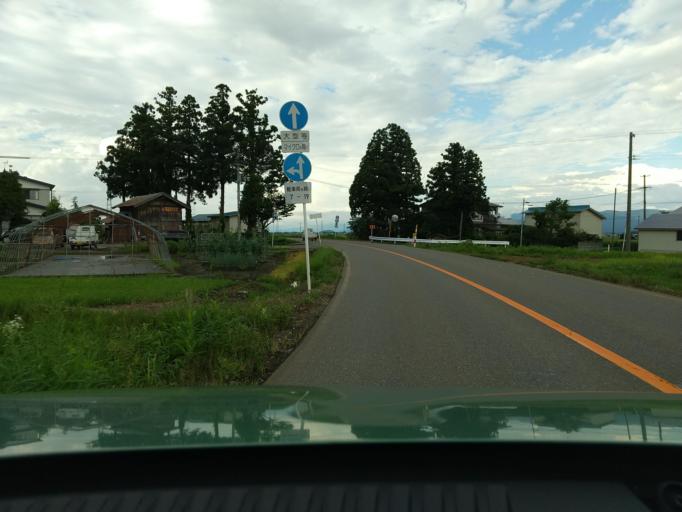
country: JP
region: Akita
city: Yokotemachi
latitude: 39.3048
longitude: 140.4903
